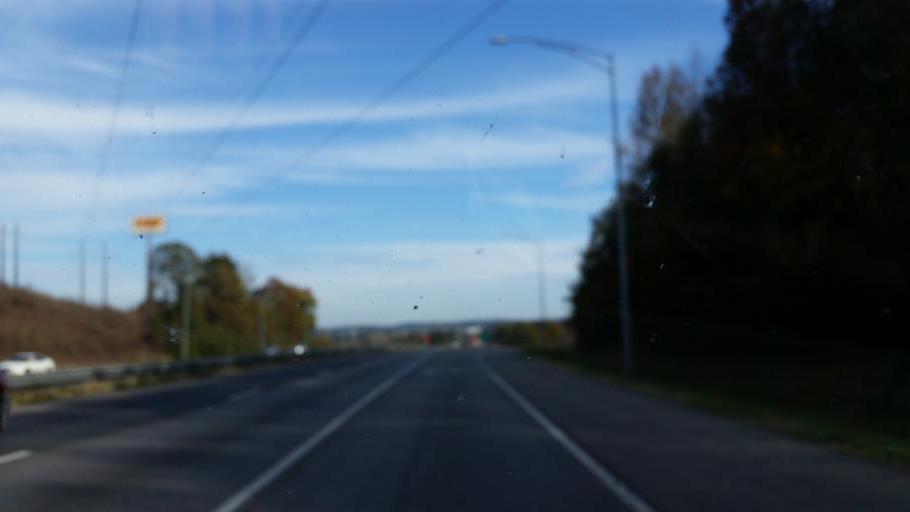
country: US
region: Alabama
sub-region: Tuscaloosa County
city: Holt
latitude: 33.1750
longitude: -87.4807
